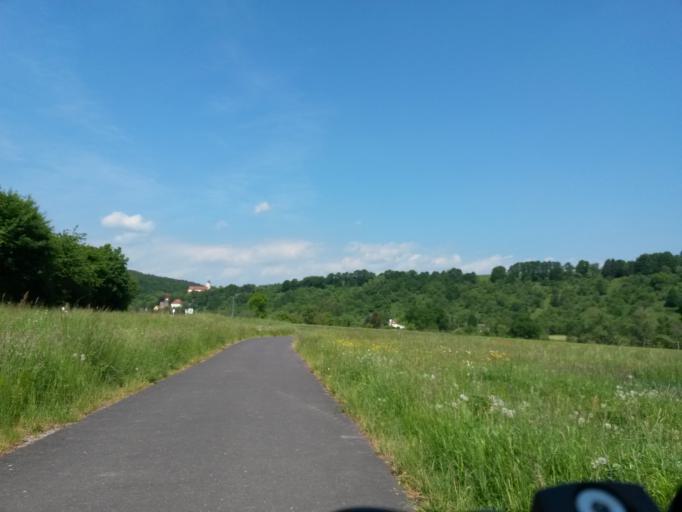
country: DE
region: Bavaria
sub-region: Regierungsbezirk Unterfranken
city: Euerdorf
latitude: 50.1619
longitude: 10.0167
